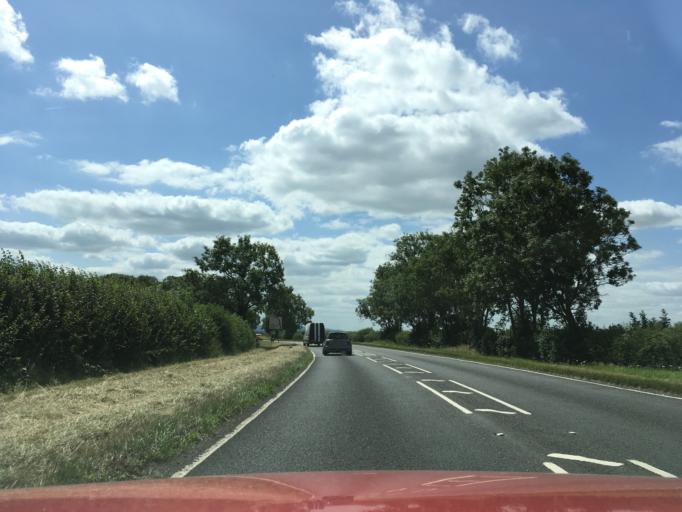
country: GB
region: England
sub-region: Buckinghamshire
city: Aylesbury
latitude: 51.8538
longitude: -0.8290
